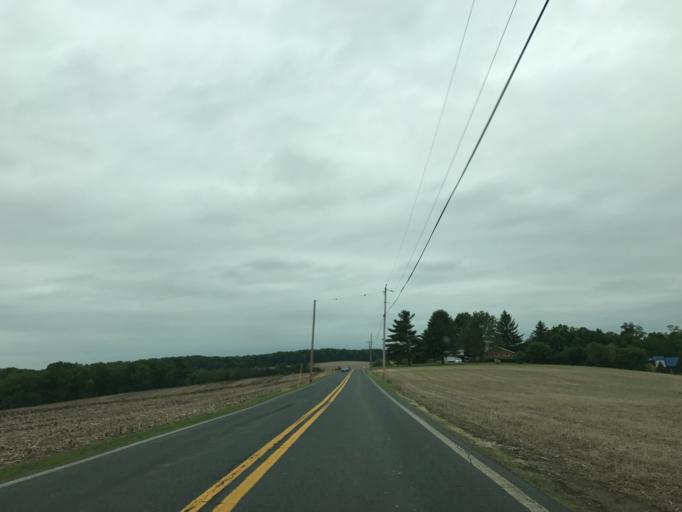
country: US
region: Maryland
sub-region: Carroll County
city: Hampstead
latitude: 39.5978
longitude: -76.8780
